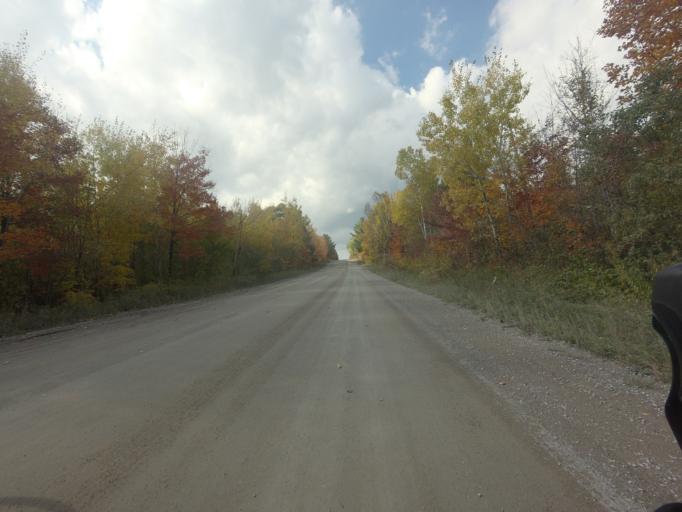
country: CA
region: Ontario
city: Petawawa
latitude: 45.8181
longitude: -77.3897
